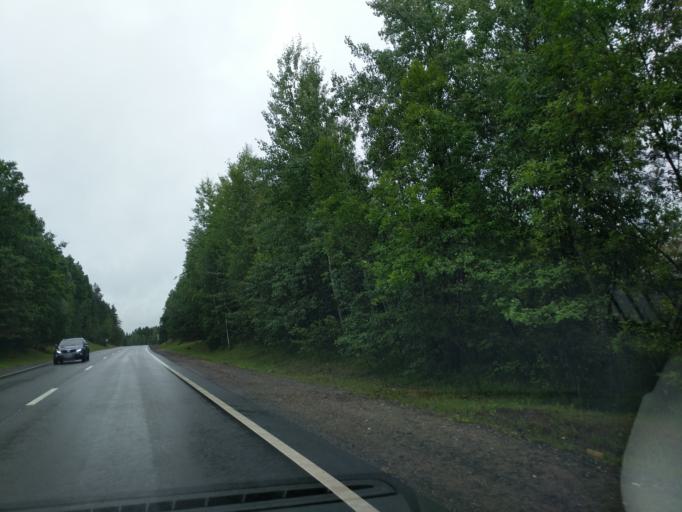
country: BY
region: Minsk
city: Syomkava
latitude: 54.1898
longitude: 27.4998
